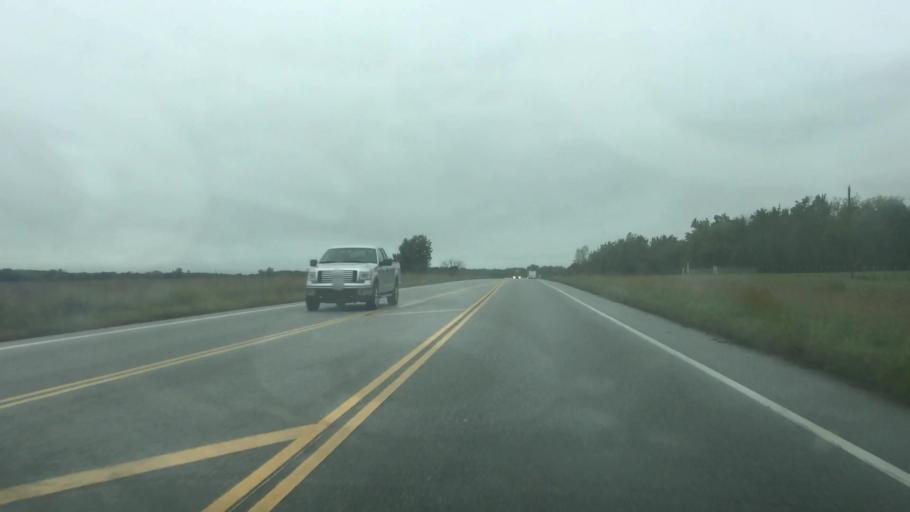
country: US
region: Kansas
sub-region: Anderson County
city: Garnett
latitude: 38.2645
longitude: -95.2429
